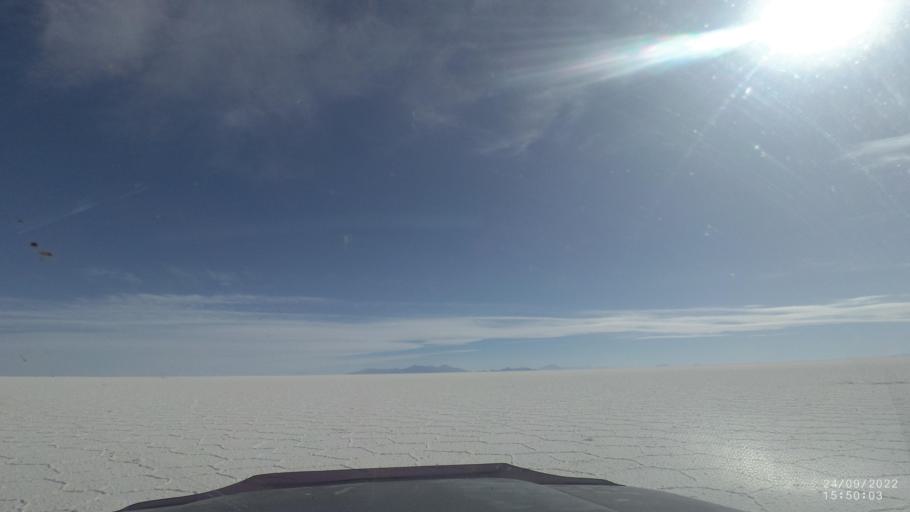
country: BO
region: Potosi
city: Colchani
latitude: -20.3060
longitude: -67.2468
